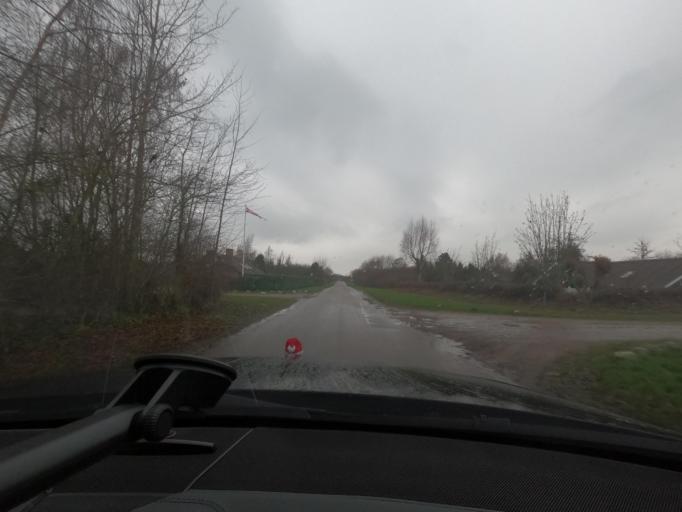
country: DK
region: South Denmark
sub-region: Sonderborg Kommune
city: Horuphav
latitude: 54.8762
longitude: 10.0163
